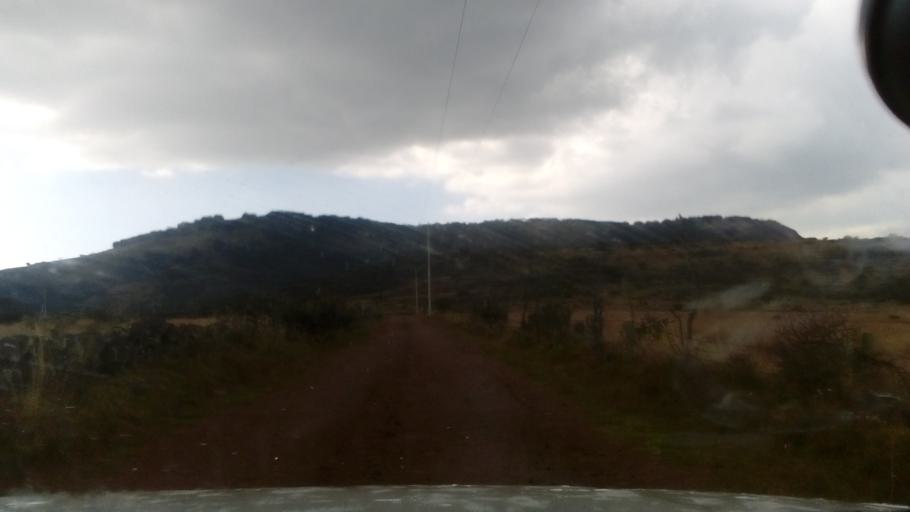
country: MX
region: Guanajuato
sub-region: Silao de la Victoria
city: San Francisco (Banos de Agua Caliente)
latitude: 21.1601
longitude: -101.4308
